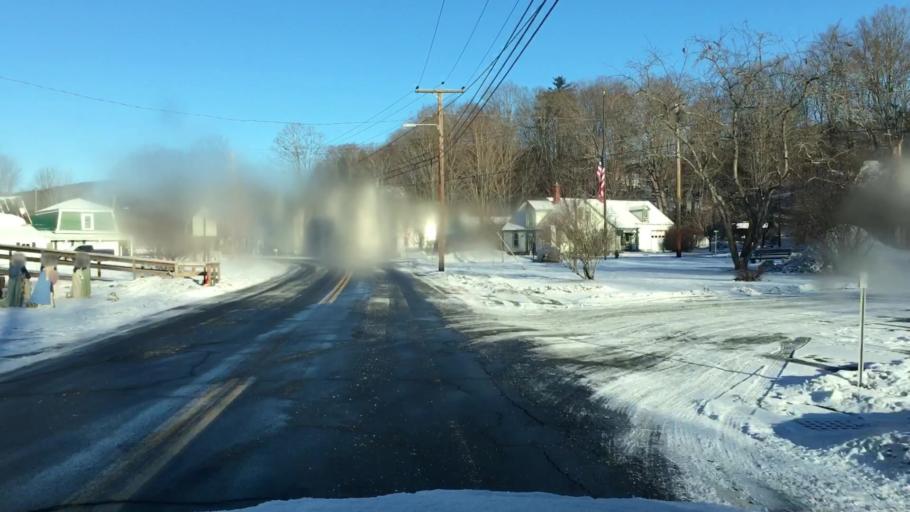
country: US
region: New Hampshire
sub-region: Grafton County
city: Woodsville
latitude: 44.2598
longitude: -72.0534
